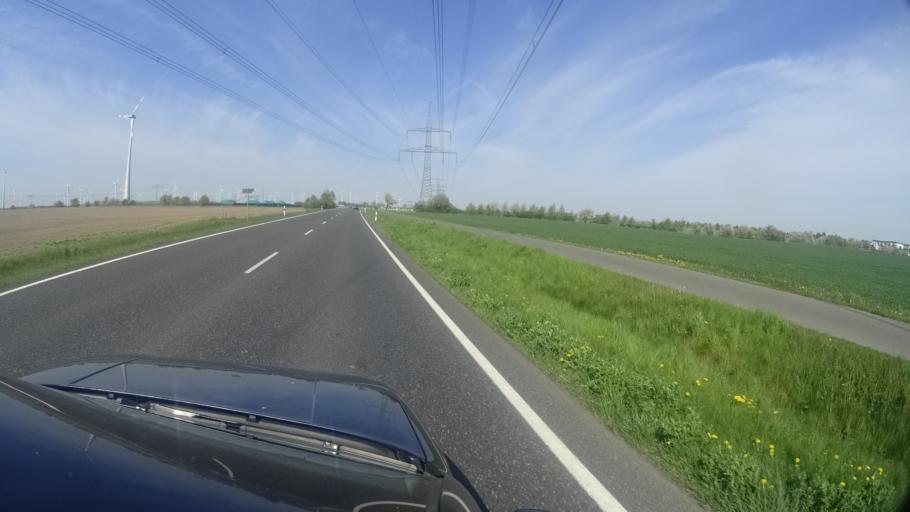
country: DE
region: Brandenburg
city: Nauen
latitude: 52.5941
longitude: 12.8674
